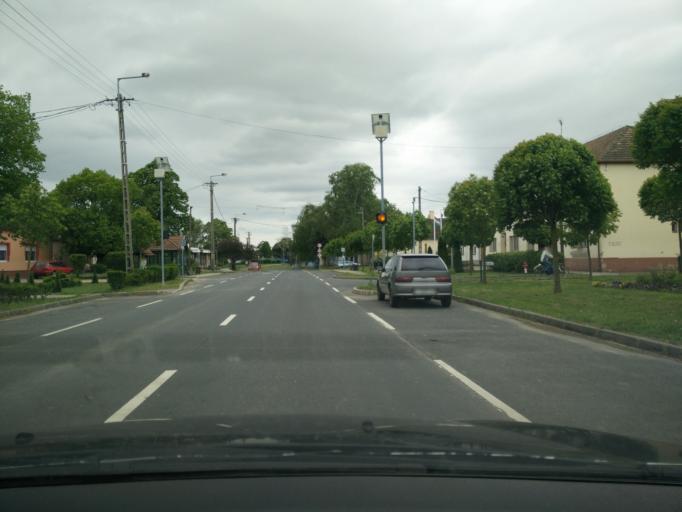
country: HU
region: Zala
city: Turje
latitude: 46.9836
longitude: 17.1050
